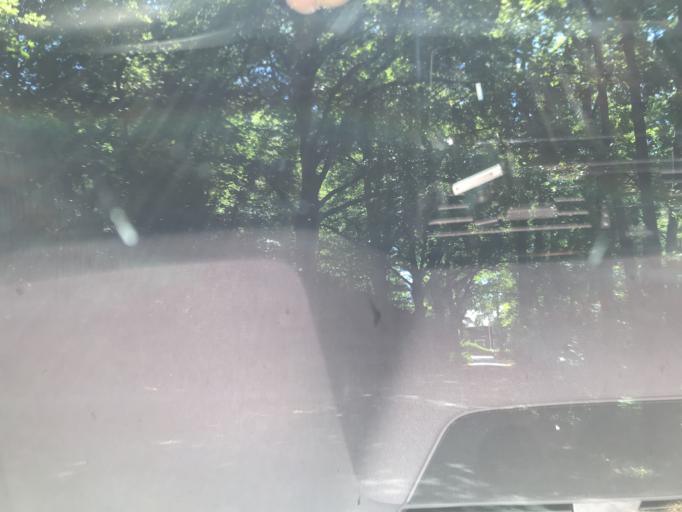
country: NL
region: North Holland
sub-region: Gemeente Naarden
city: Naarden
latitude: 52.2939
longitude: 5.1905
